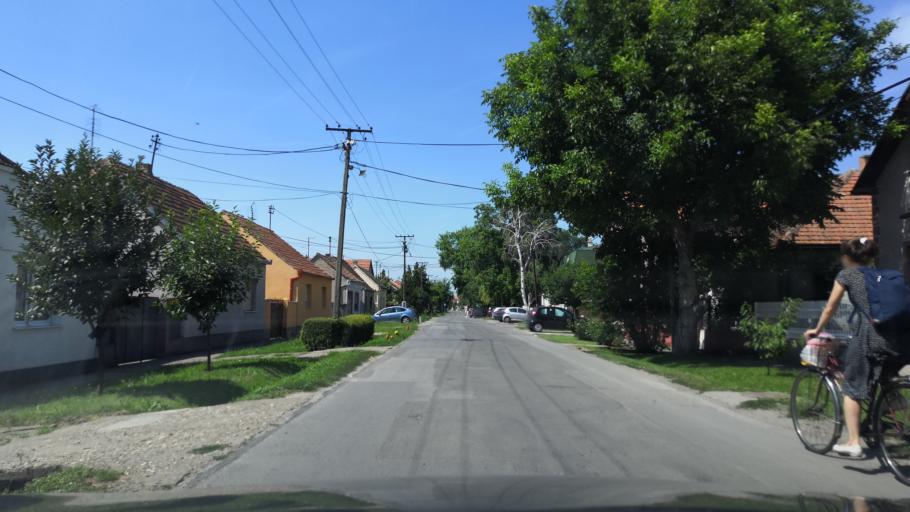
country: RS
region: Autonomna Pokrajina Vojvodina
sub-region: Sremski Okrug
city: Stara Pazova
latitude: 44.9839
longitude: 20.1433
